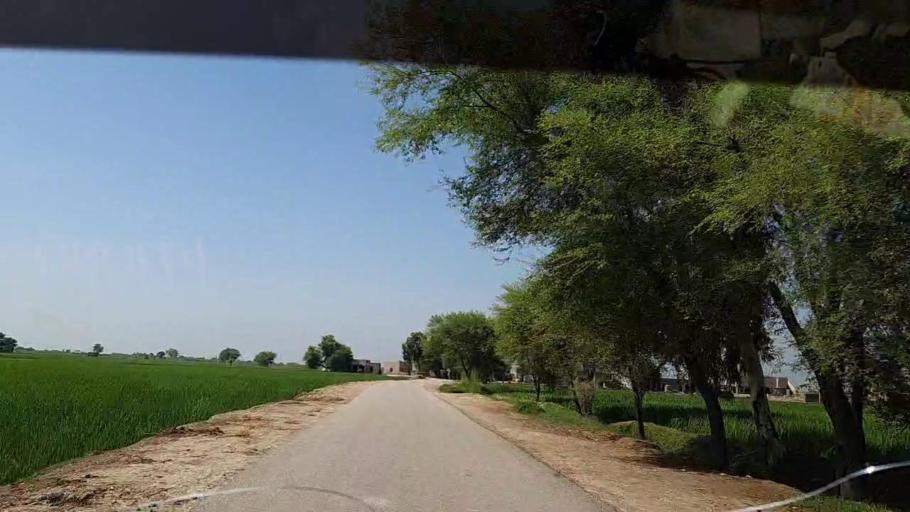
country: PK
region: Sindh
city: Kandhkot
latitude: 28.3091
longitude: 69.1051
